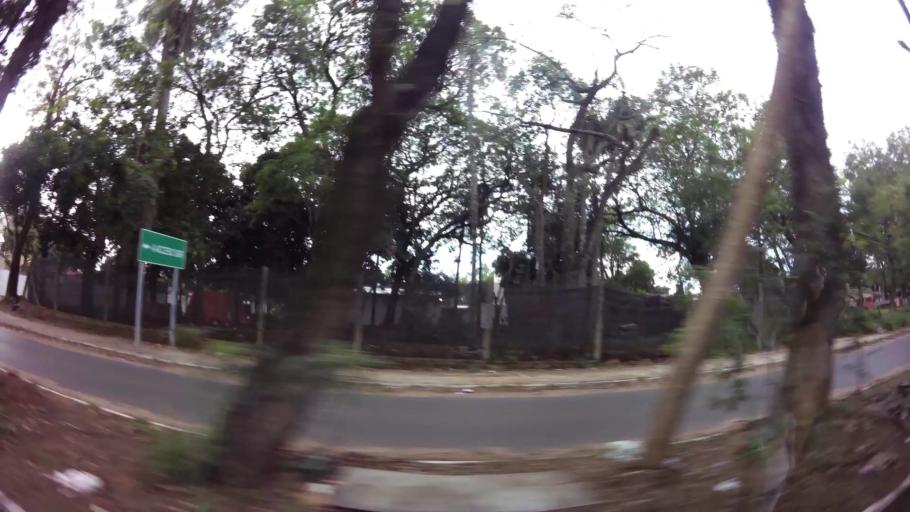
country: PY
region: Central
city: Fernando de la Mora
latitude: -25.3360
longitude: -57.5560
